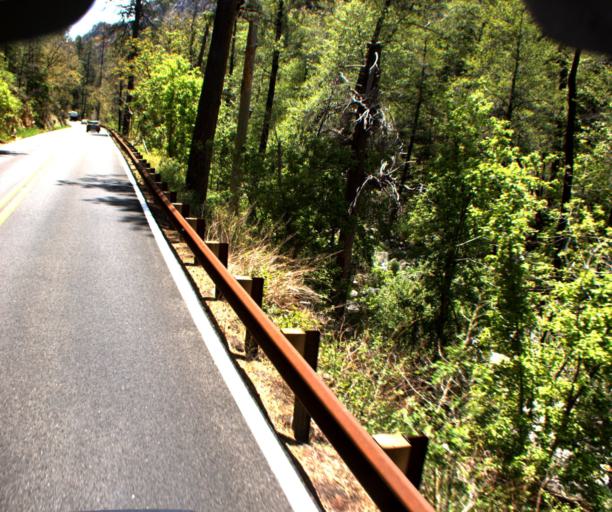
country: US
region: Arizona
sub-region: Coconino County
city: Kachina Village
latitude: 35.0208
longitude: -111.7365
